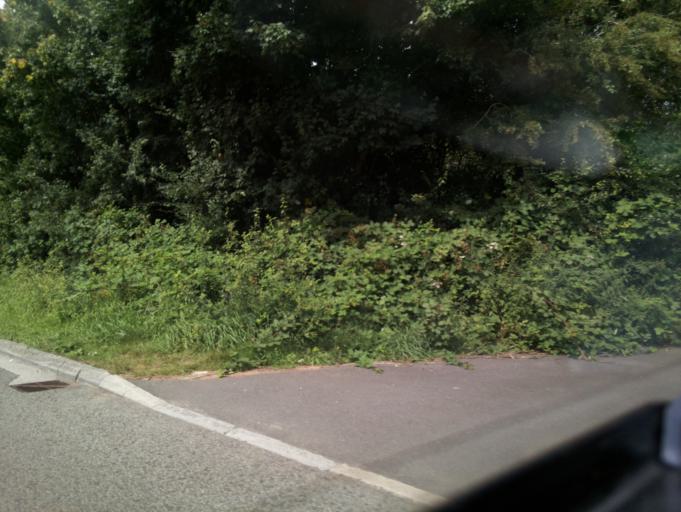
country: GB
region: England
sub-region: Somerset
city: Glastonbury
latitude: 51.1586
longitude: -2.7129
